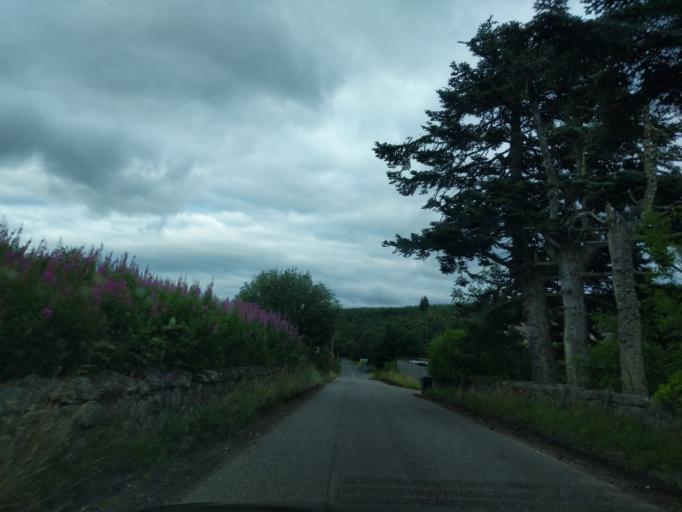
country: GB
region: Scotland
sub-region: Aberdeenshire
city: Aboyne
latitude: 57.0701
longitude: -2.8556
